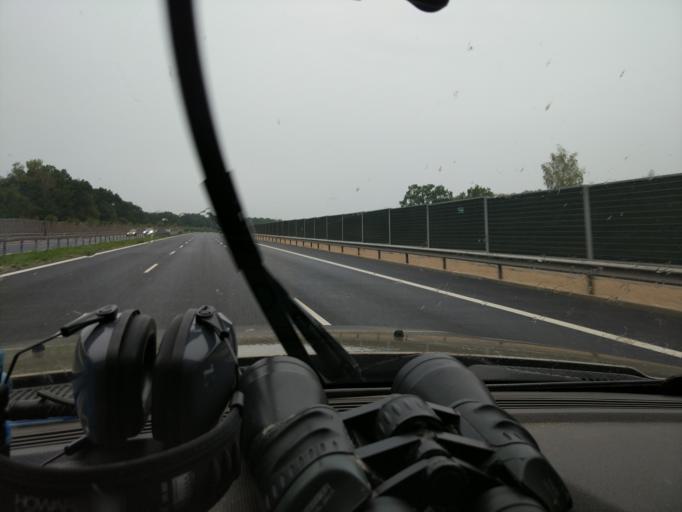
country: PL
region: Masovian Voivodeship
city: Zielonka
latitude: 52.3417
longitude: 21.1565
